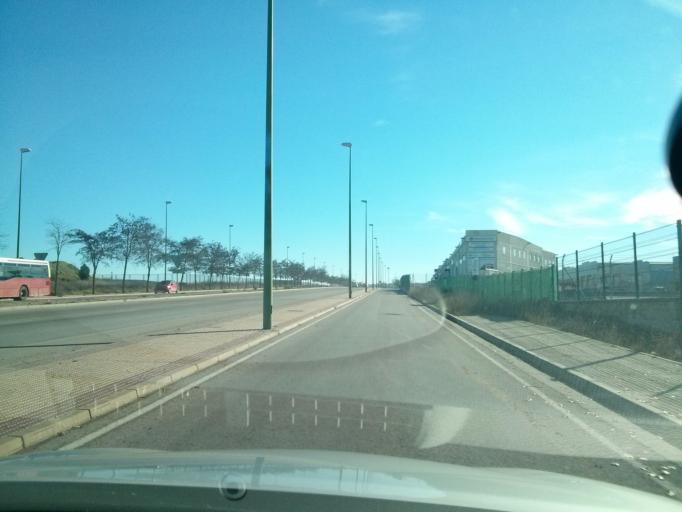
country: ES
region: Castille and Leon
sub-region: Provincia de Burgos
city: Sotragero
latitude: 42.3743
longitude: -3.7219
